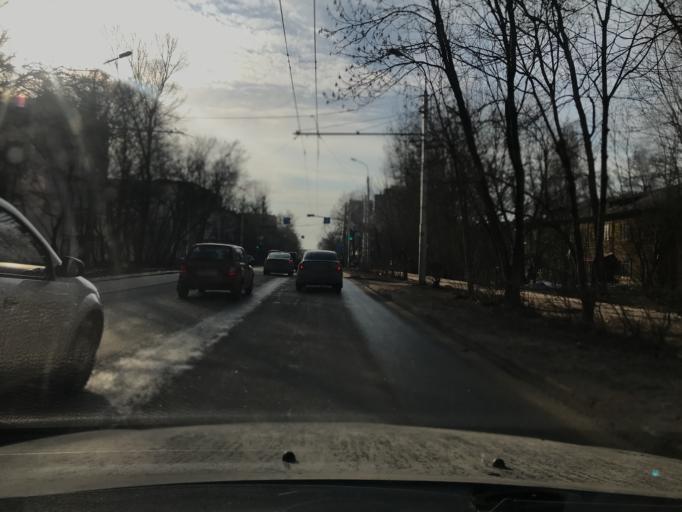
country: RU
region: Kaluga
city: Kaluga
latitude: 54.5215
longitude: 36.2554
